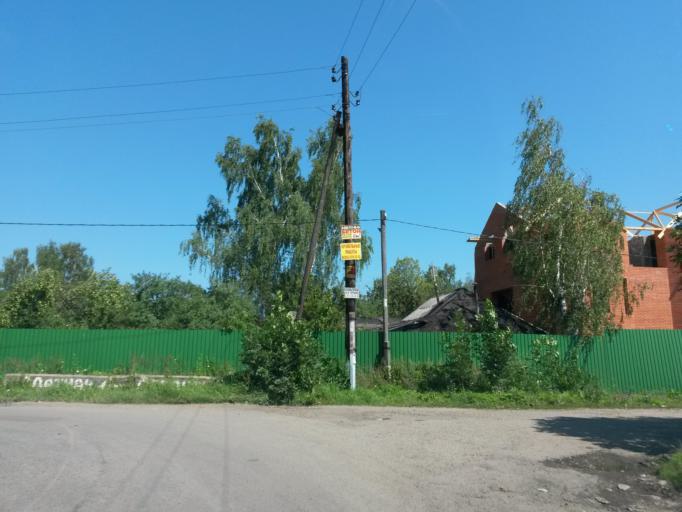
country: RU
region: Moskovskaya
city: Stolbovaya
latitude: 55.2563
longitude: 37.4864
